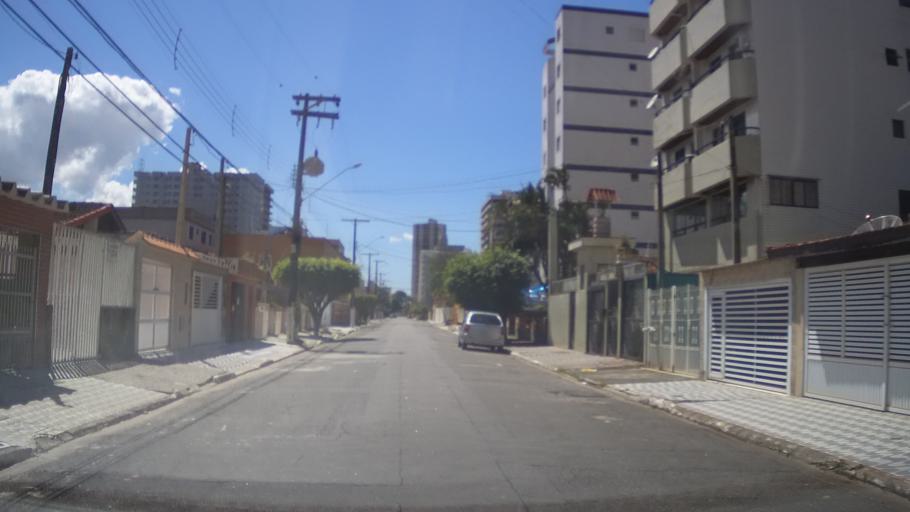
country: BR
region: Sao Paulo
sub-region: Mongagua
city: Mongagua
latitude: -24.0511
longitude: -46.5333
